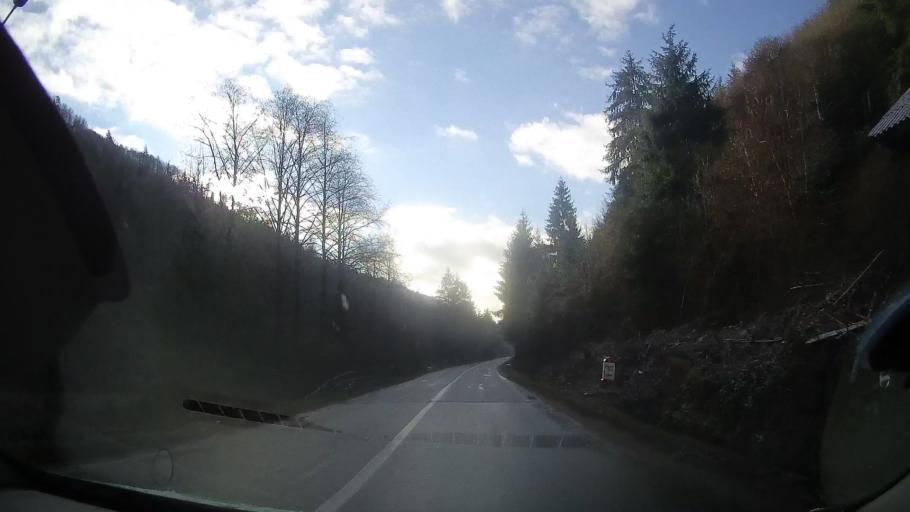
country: RO
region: Alba
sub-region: Comuna Albac
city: Albac
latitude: 46.4396
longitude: 22.9674
